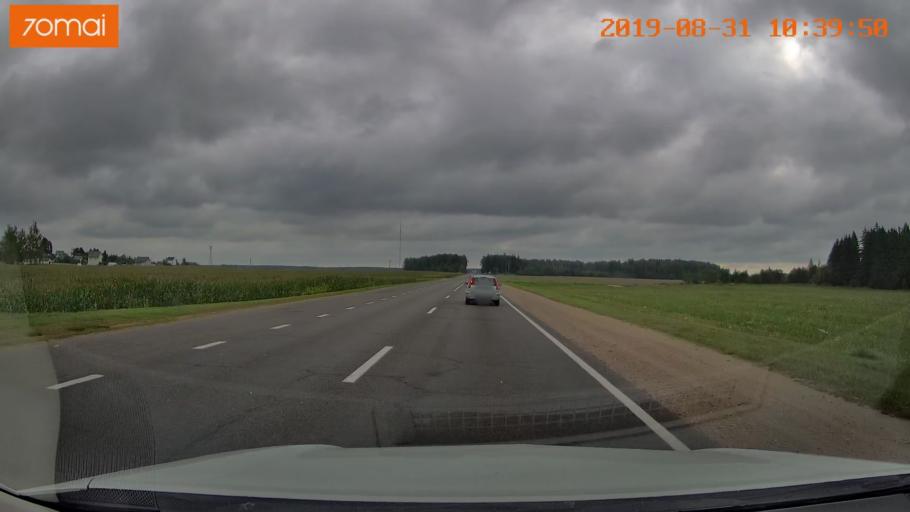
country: BY
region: Mogilev
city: Palykavichy Pyershyya
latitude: 53.9734
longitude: 30.2790
